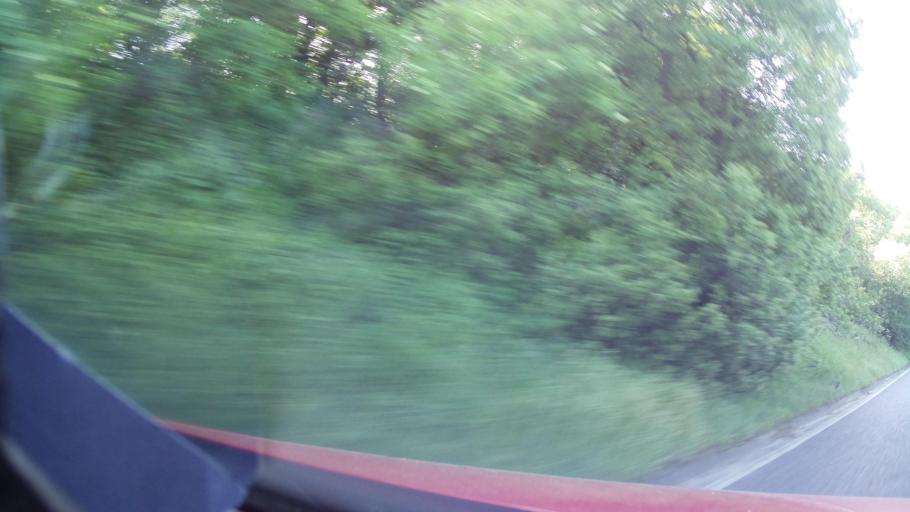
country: GB
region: England
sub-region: Somerset
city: Yeovil
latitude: 50.9454
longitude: -2.6881
